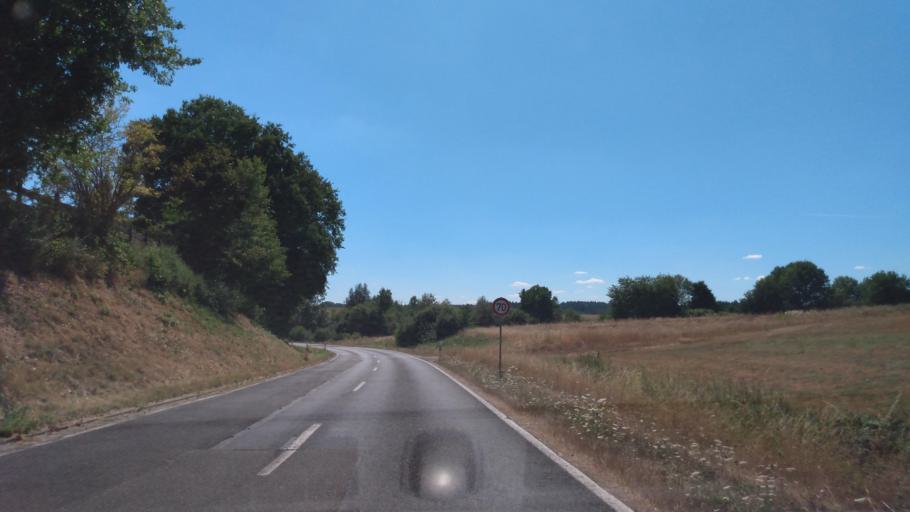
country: DE
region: Rheinland-Pfalz
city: Grosslittgen
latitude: 50.0228
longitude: 6.7905
